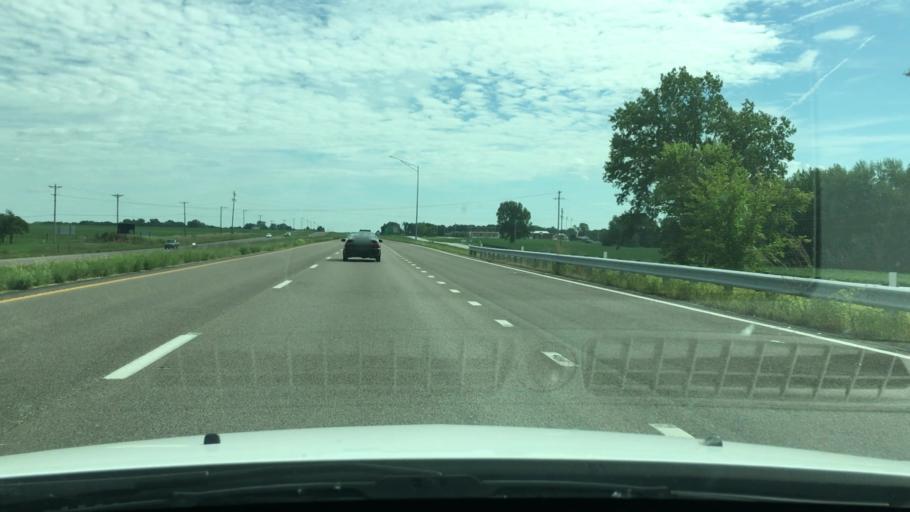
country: US
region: Missouri
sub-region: Callaway County
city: Fulton
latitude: 38.9593
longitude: -91.9275
